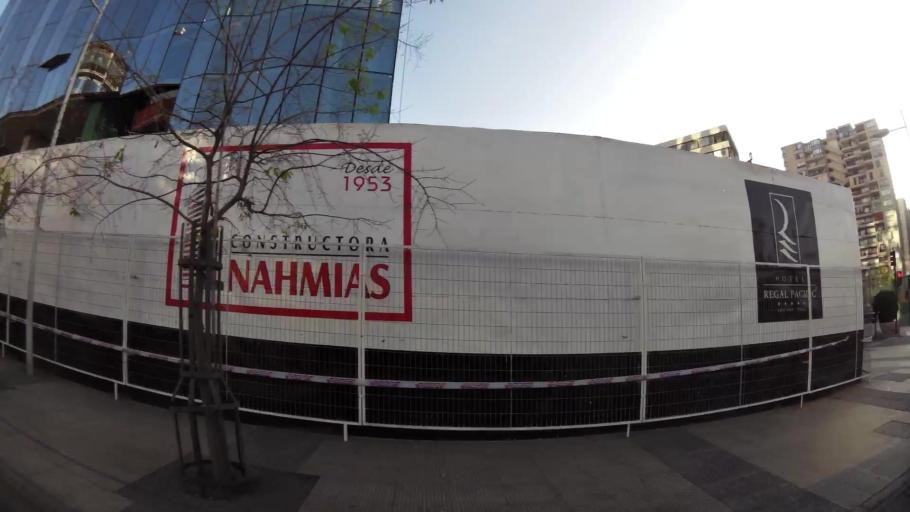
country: CL
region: Santiago Metropolitan
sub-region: Provincia de Santiago
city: Villa Presidente Frei, Nunoa, Santiago, Chile
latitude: -33.4079
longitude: -70.5678
